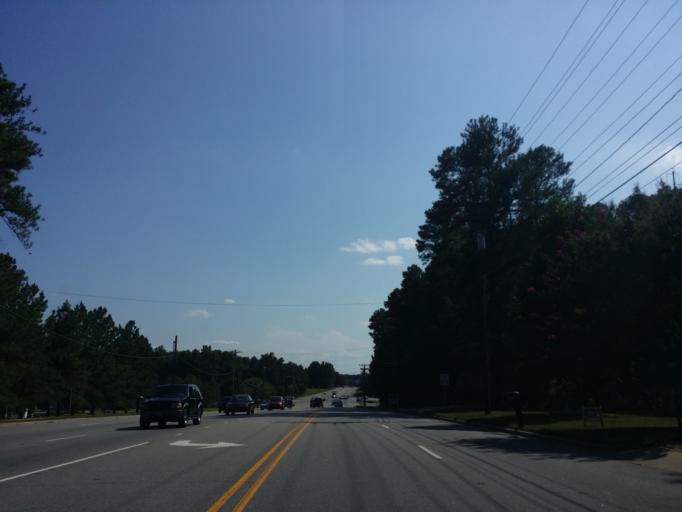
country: US
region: North Carolina
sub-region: Durham County
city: Durham
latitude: 35.9269
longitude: -78.8454
